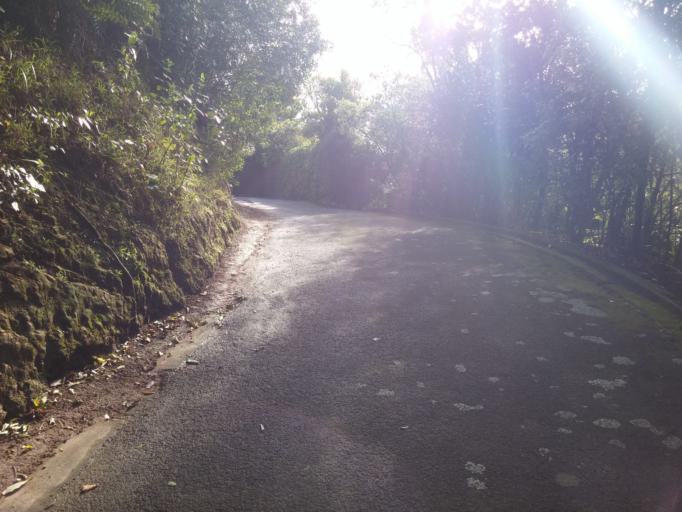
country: NZ
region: Wellington
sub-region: Wellington City
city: Brooklyn
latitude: -41.3227
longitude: 174.7852
